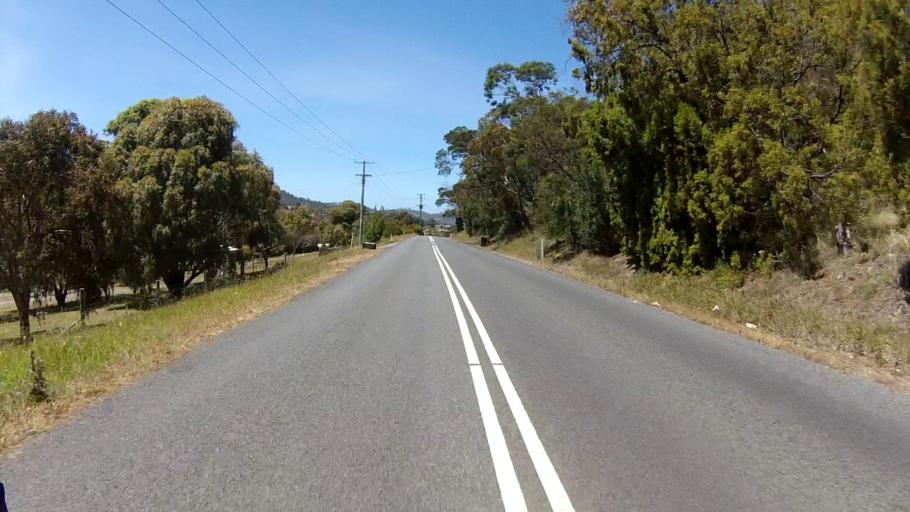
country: AU
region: Tasmania
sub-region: Clarence
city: Howrah
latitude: -42.8627
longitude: 147.4174
